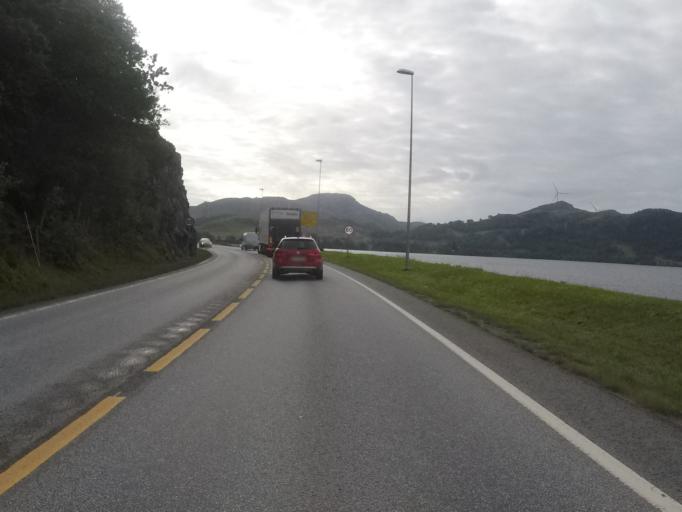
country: NO
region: Rogaland
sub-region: Gjesdal
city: Algard
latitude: 58.7655
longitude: 5.8740
